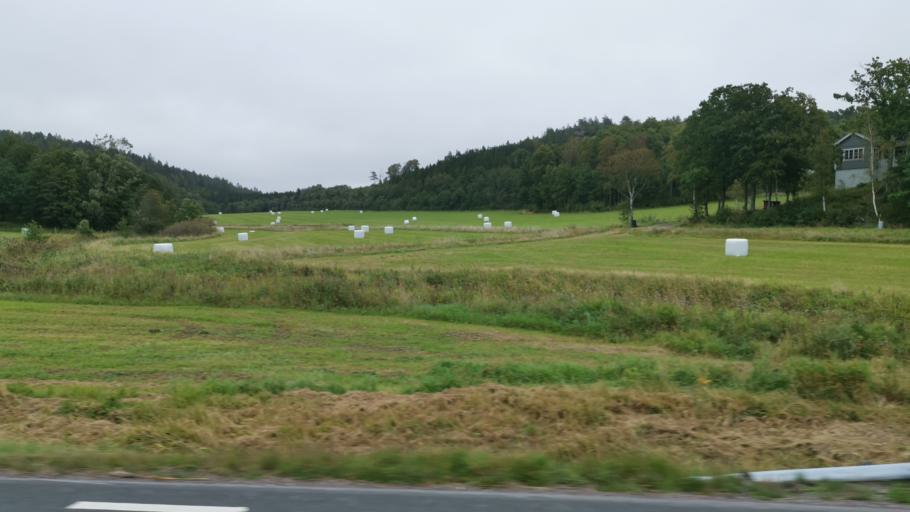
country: SE
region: Vaestra Goetaland
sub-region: Sotenas Kommun
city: Hunnebostrand
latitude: 58.5505
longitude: 11.4110
